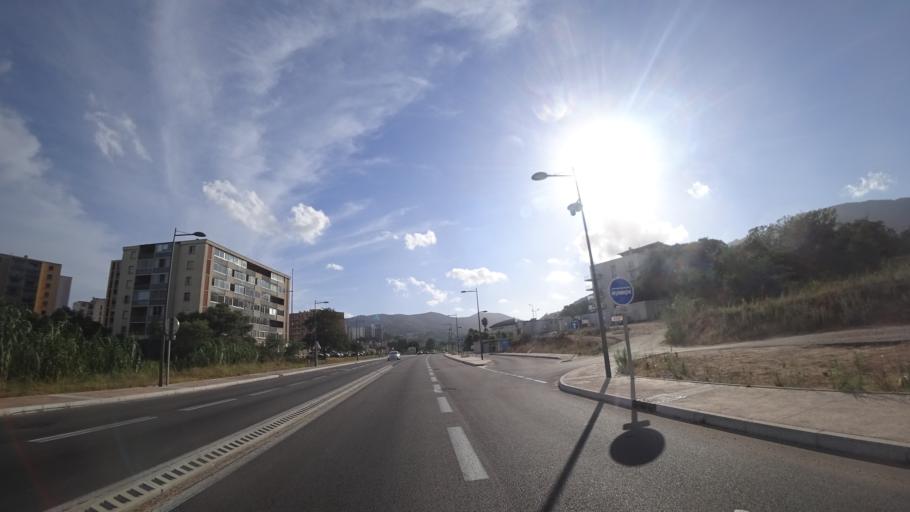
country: FR
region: Corsica
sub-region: Departement de la Corse-du-Sud
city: Ajaccio
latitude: 41.9386
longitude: 8.7413
